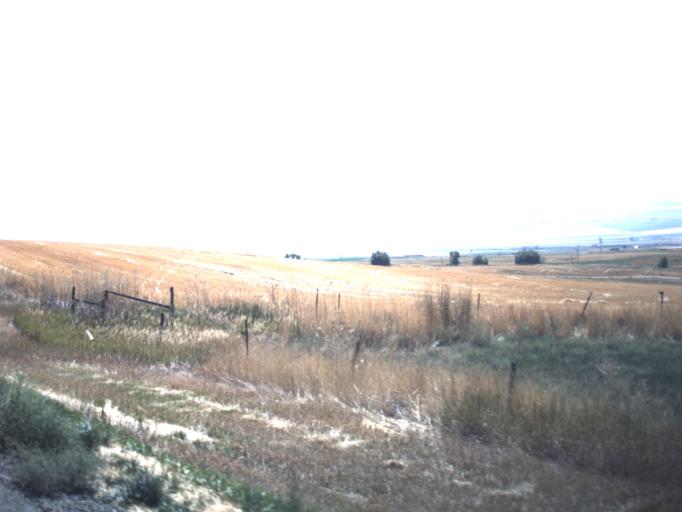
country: US
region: Utah
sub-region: Cache County
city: Benson
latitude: 41.8594
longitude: -111.9773
